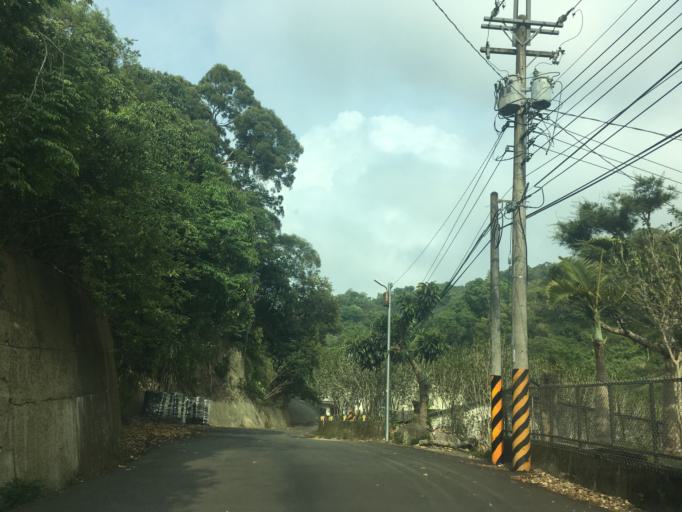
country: TW
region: Taiwan
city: Fengyuan
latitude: 24.2268
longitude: 120.7583
